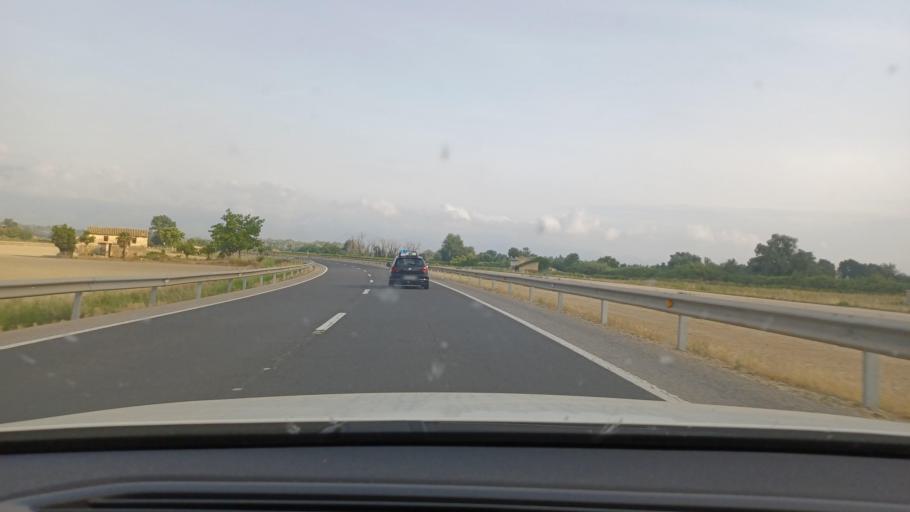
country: ES
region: Catalonia
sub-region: Provincia de Tarragona
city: Tortosa
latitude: 40.7736
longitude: 0.5272
